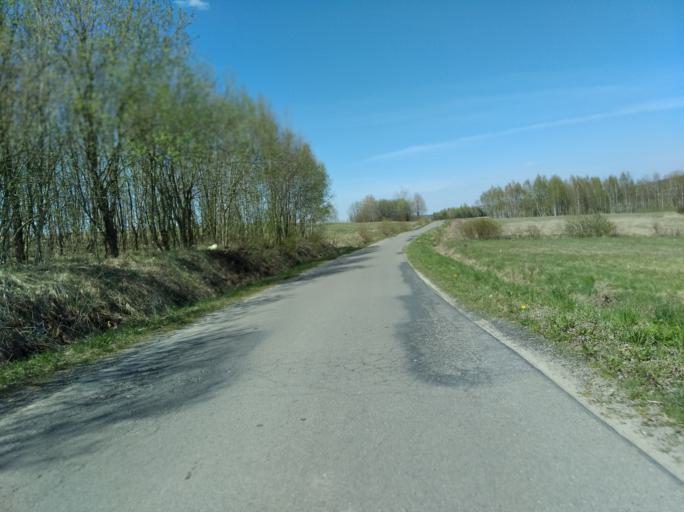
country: PL
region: Subcarpathian Voivodeship
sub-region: Powiat brzozowski
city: Jablonka
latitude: 49.7369
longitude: 22.1145
